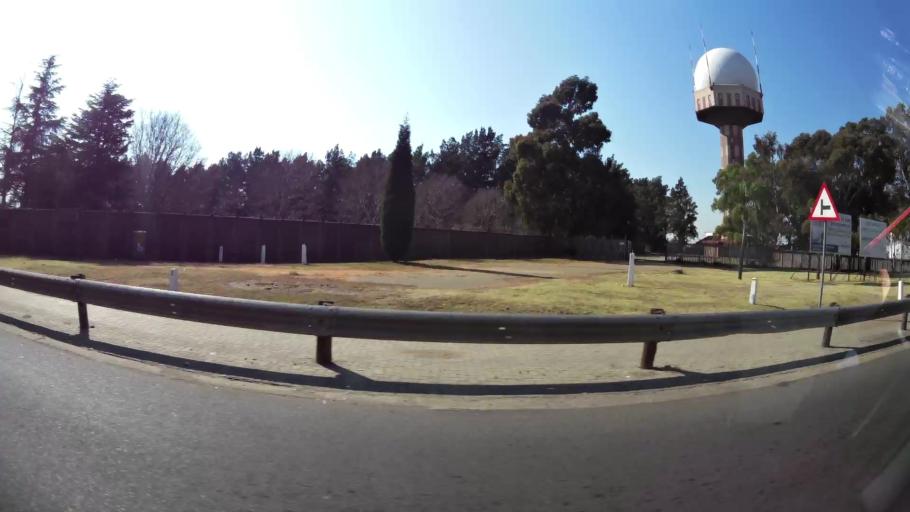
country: ZA
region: Gauteng
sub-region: Ekurhuleni Metropolitan Municipality
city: Boksburg
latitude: -26.1496
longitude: 28.2236
